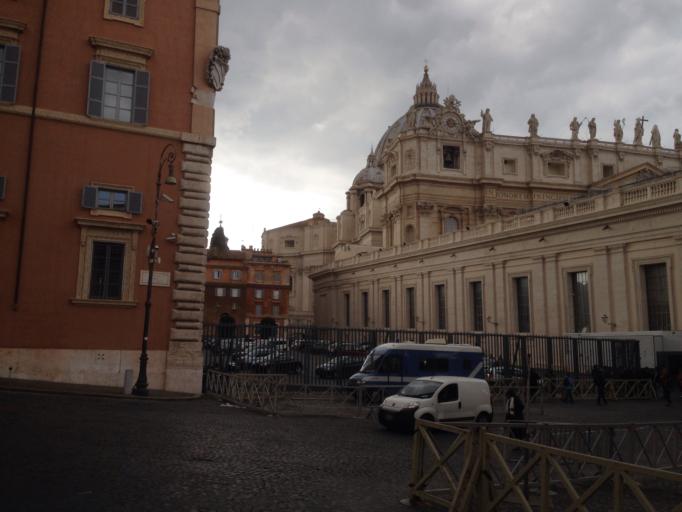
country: VA
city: Vatican City
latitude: 41.9012
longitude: 12.4566
